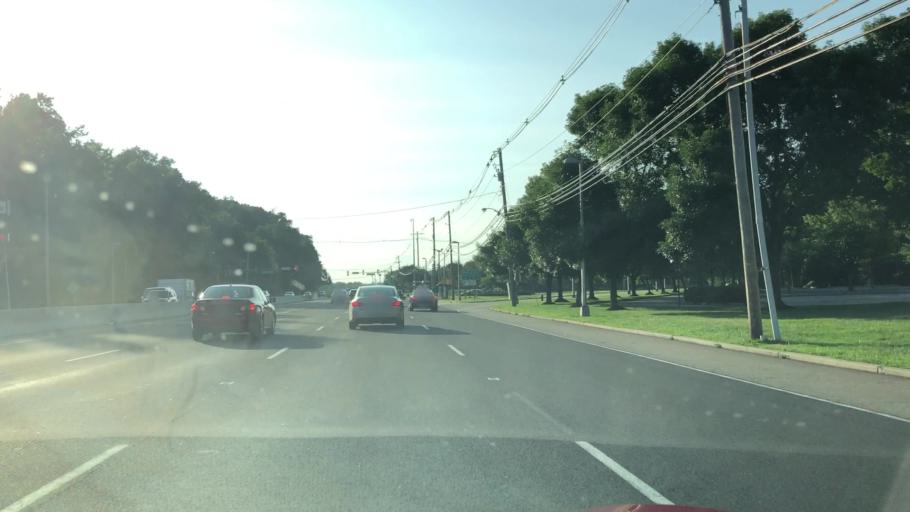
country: US
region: New Jersey
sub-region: Morris County
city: Morris Plains
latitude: 40.8581
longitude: -74.4880
